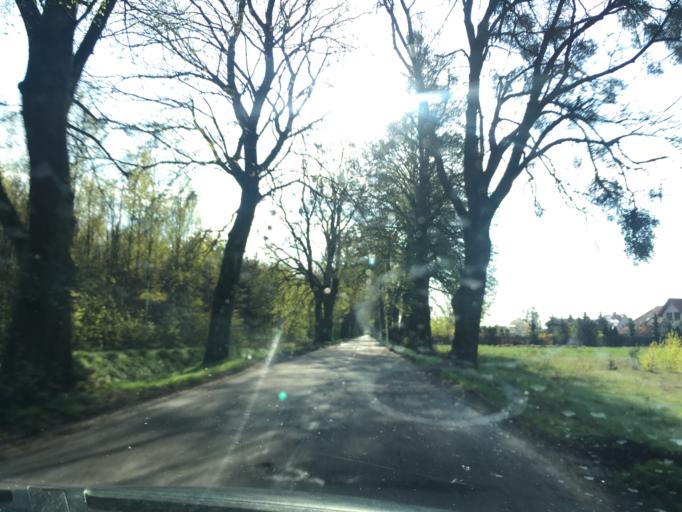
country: PL
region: Warmian-Masurian Voivodeship
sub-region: Powiat nidzicki
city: Nidzica
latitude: 53.4336
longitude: 20.3711
